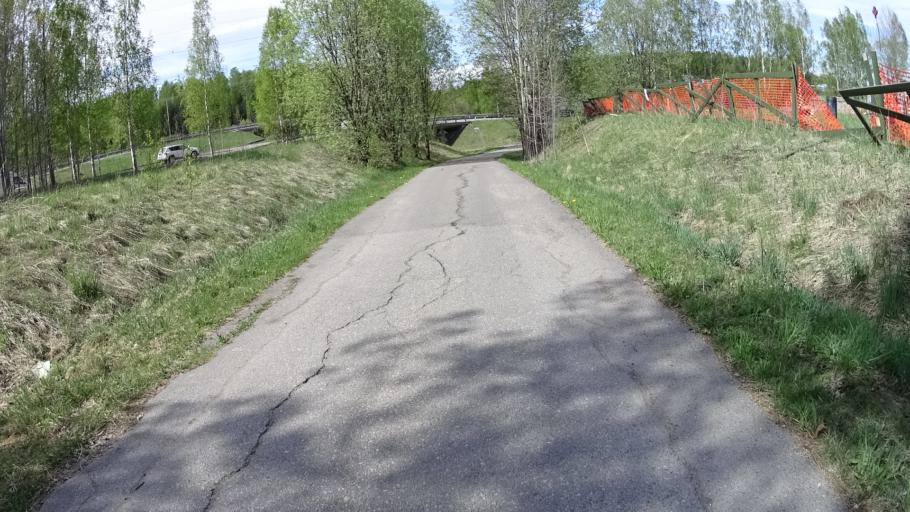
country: FI
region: Uusimaa
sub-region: Helsinki
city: Kilo
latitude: 60.2731
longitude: 24.8062
